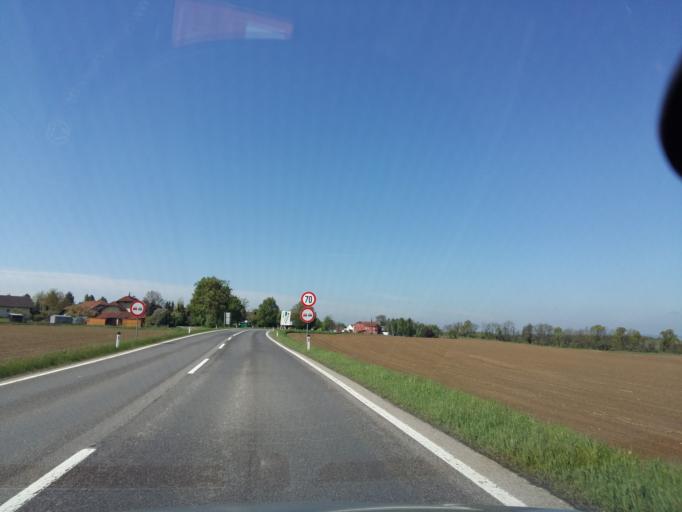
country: AT
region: Upper Austria
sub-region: Politischer Bezirk Scharding
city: Sankt Florian am Inn
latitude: 48.4214
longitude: 13.4438
